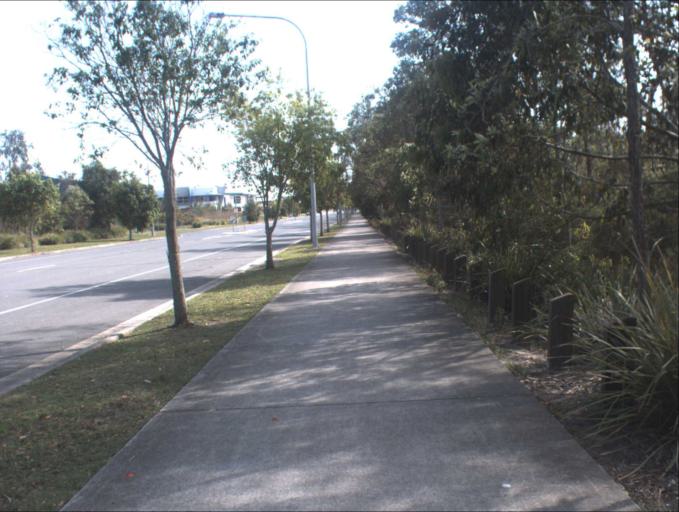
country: AU
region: Queensland
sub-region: Logan
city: Woodridge
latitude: -27.6740
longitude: 153.0794
